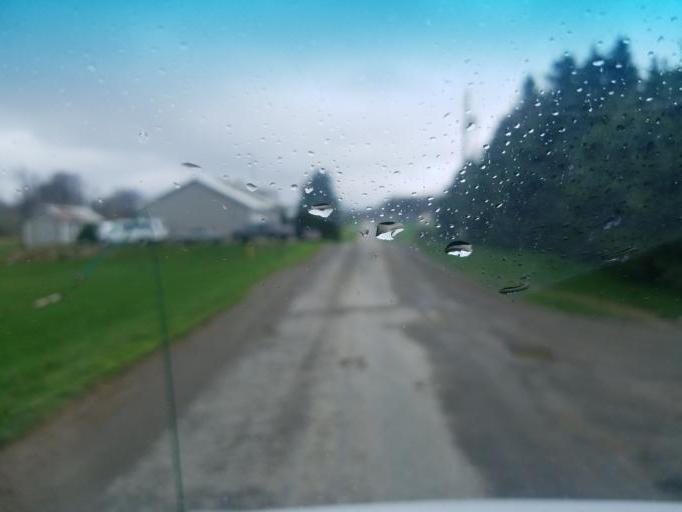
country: US
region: Ohio
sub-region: Richland County
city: Shelby
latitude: 40.9191
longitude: -82.5952
